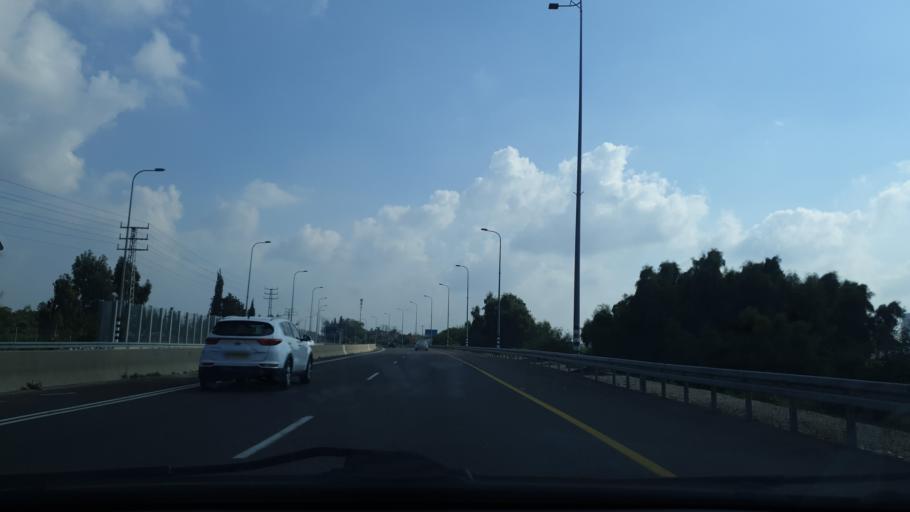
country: IL
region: Central District
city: Ramla
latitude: 31.9487
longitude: 34.8579
